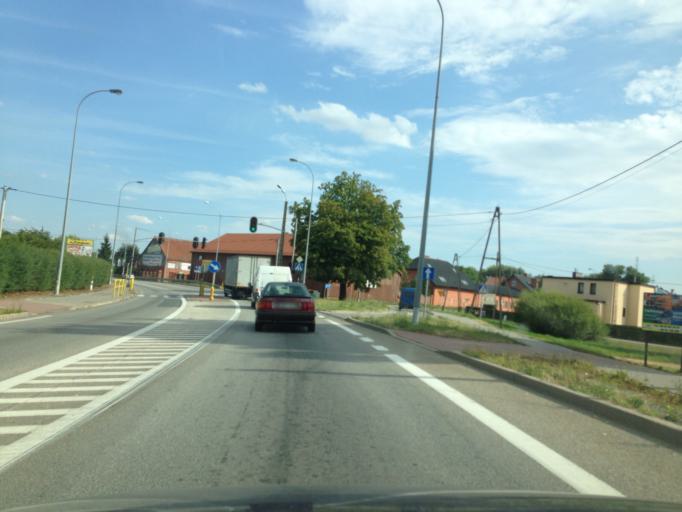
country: PL
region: Pomeranian Voivodeship
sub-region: Powiat gdanski
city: Pszczolki
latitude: 54.1747
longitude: 18.6918
